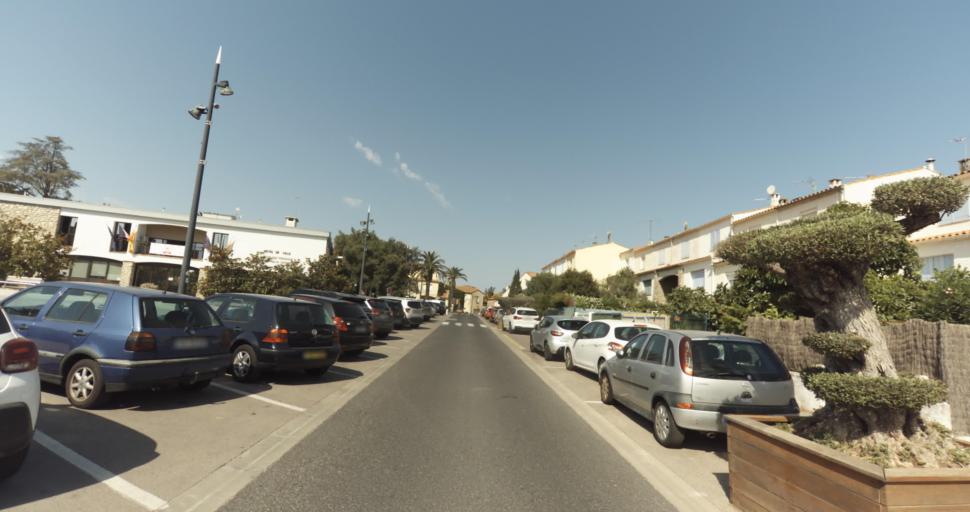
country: FR
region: Languedoc-Roussillon
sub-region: Departement des Pyrenees-Orientales
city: Latour-Bas-Elne
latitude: 42.6178
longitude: 3.0044
